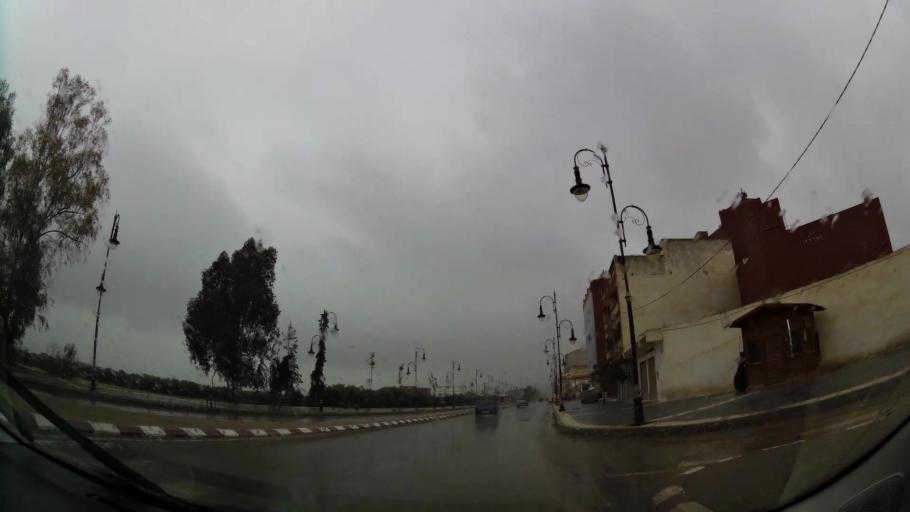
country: MA
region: Taza-Al Hoceima-Taounate
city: Imzourene
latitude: 35.1147
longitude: -3.8419
